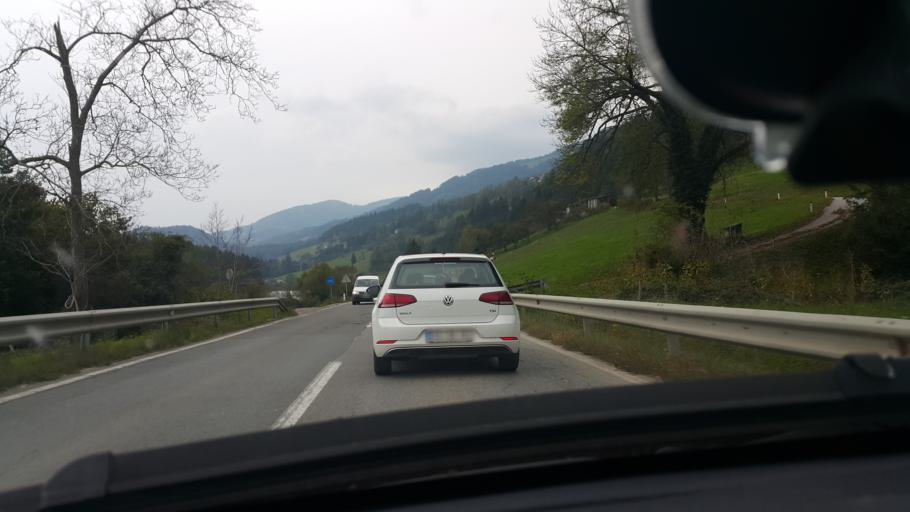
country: SI
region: Muta
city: Muta
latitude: 46.6155
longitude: 15.1902
